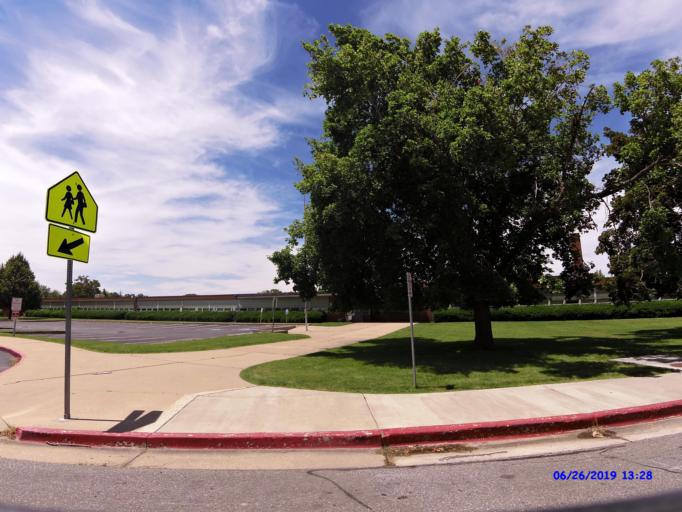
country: US
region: Utah
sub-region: Weber County
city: South Ogden
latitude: 41.2039
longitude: -111.9585
